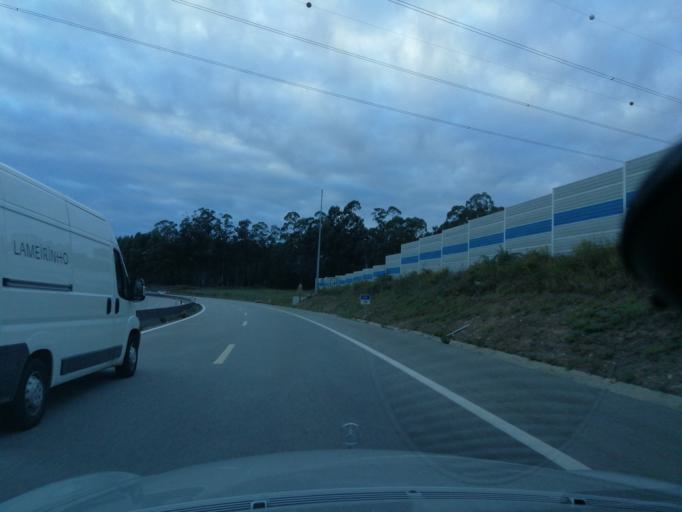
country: PT
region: Aveiro
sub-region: Albergaria-A-Velha
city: Albergaria-a-Velha
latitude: 40.6887
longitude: -8.5156
